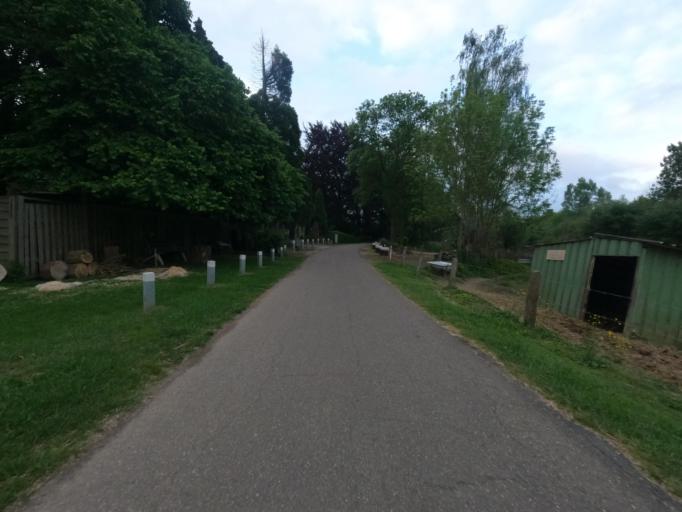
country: NL
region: Limburg
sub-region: Gemeente Roerdalen
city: Vlodrop
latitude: 51.1316
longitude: 6.0895
